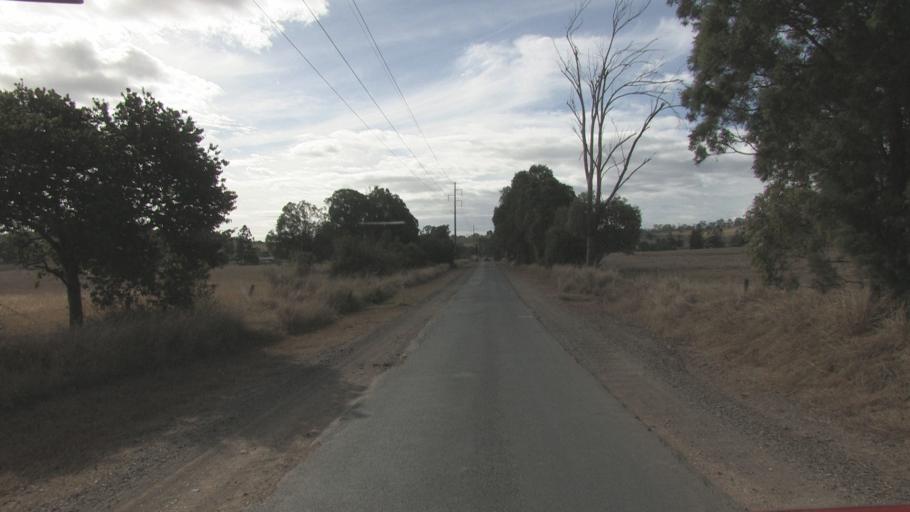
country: AU
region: Queensland
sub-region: Logan
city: Cedar Vale
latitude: -27.9201
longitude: 153.0128
